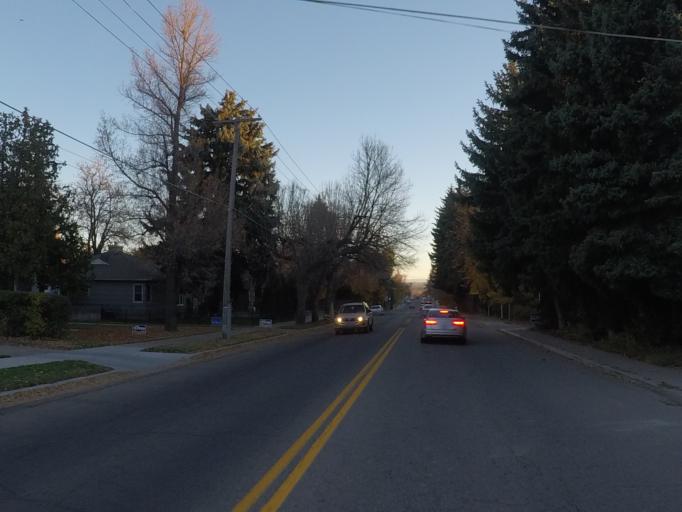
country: US
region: Montana
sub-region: Yellowstone County
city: Billings
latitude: 45.7920
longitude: -108.5279
